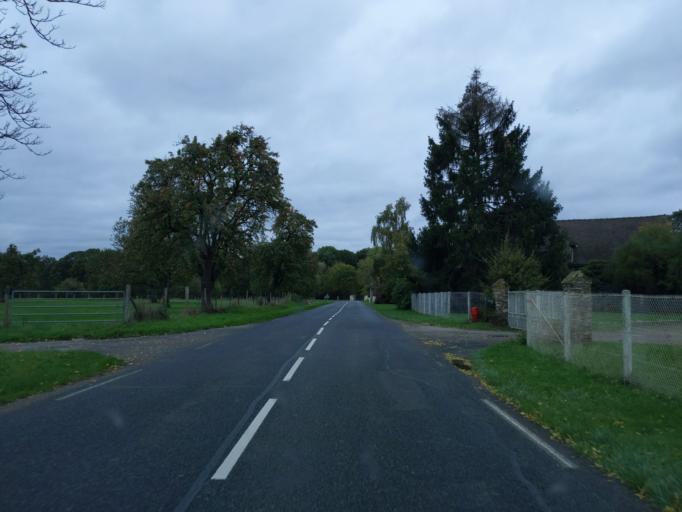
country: FR
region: Ile-de-France
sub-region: Departement des Yvelines
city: Bullion
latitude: 48.6406
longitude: 1.9874
